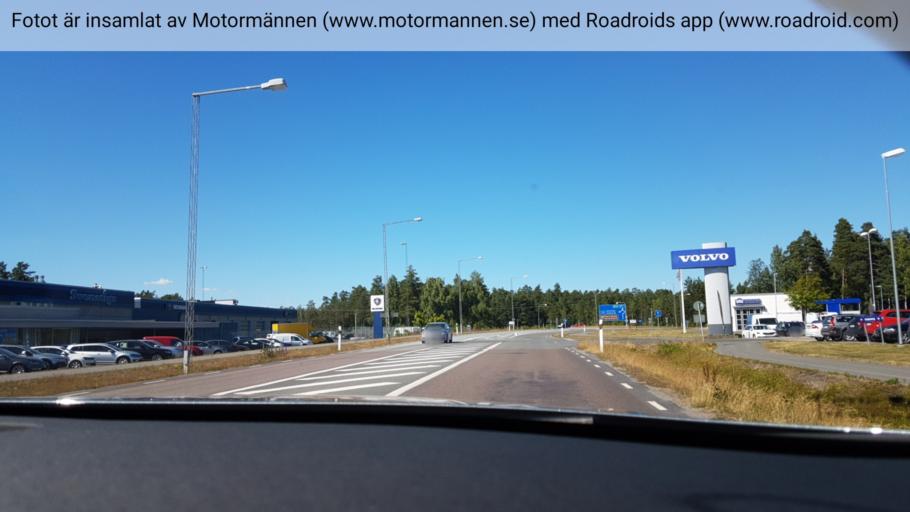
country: SE
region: Joenkoeping
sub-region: Varnamo Kommun
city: Varnamo
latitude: 57.1915
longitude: 14.0638
